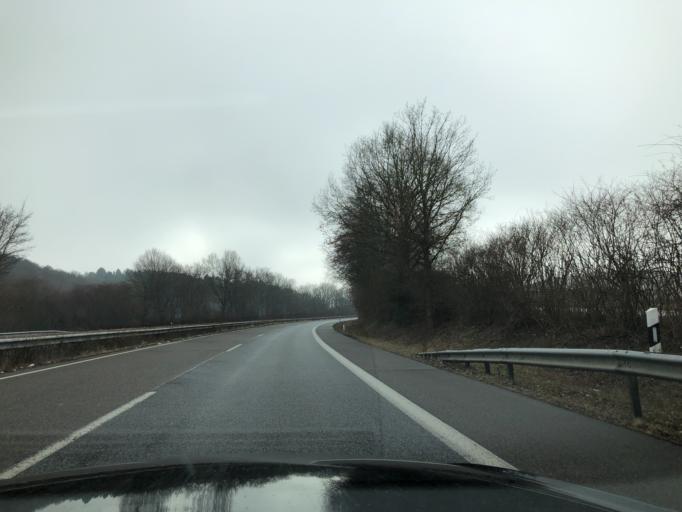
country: DE
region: Rheinland-Pfalz
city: Konigsfeld
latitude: 50.5411
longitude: 7.1969
